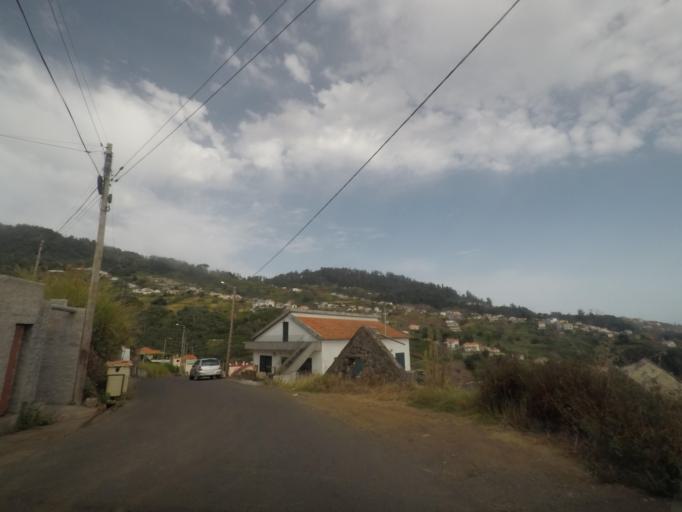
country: PT
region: Madeira
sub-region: Calheta
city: Arco da Calheta
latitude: 32.7321
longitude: -17.1554
